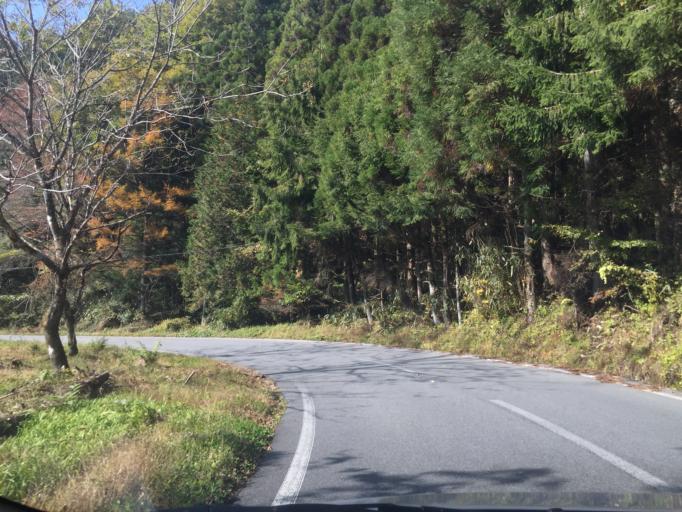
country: JP
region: Gifu
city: Nakatsugawa
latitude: 35.2113
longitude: 137.5992
